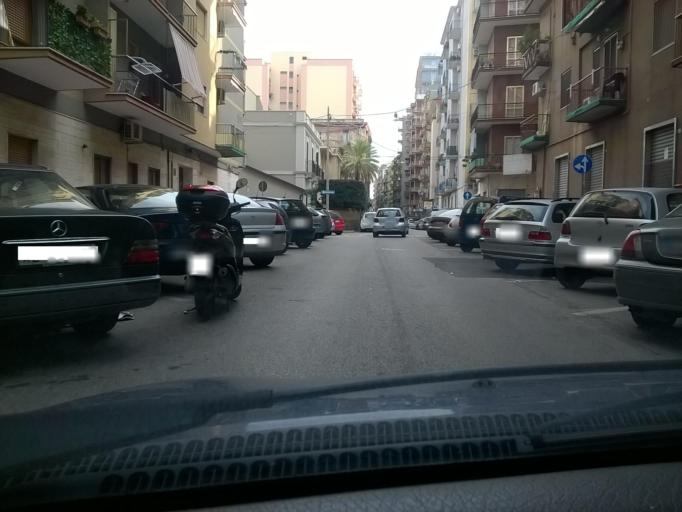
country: IT
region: Apulia
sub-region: Provincia di Taranto
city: Taranto
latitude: 40.4672
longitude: 17.2572
